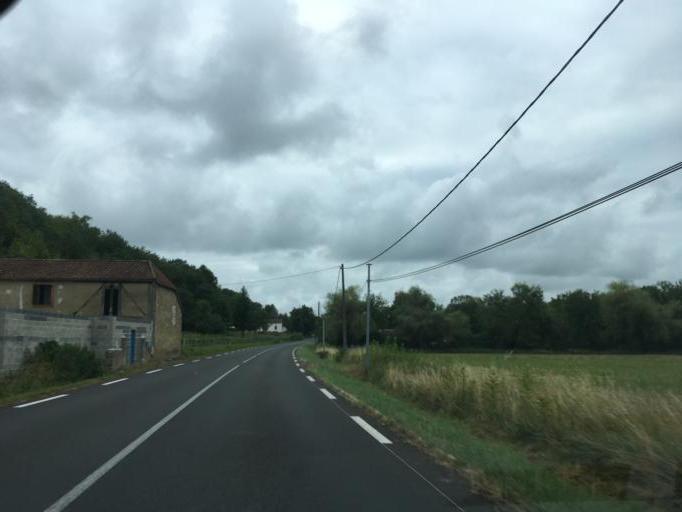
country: FR
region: Midi-Pyrenees
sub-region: Departement du Gers
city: Plaisance
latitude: 43.5827
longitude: -0.0211
